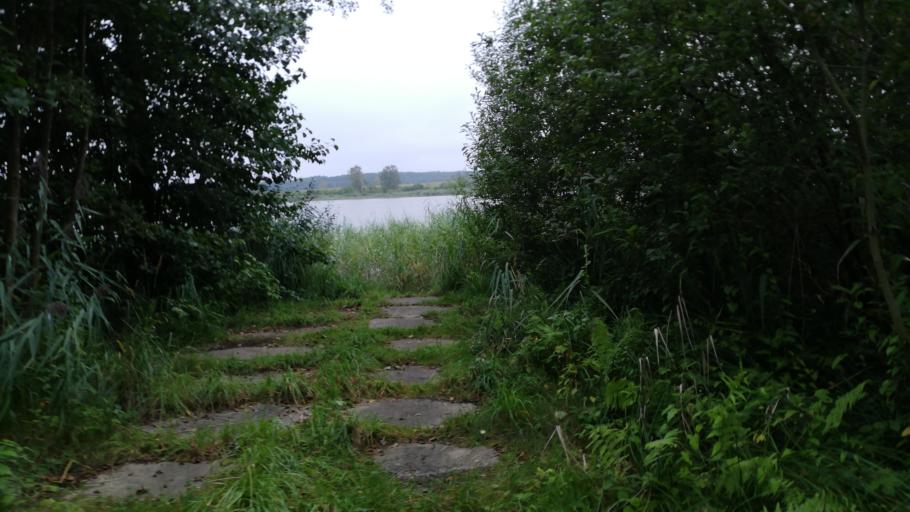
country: DE
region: Brandenburg
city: Rheinsberg
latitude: 53.0999
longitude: 12.8453
